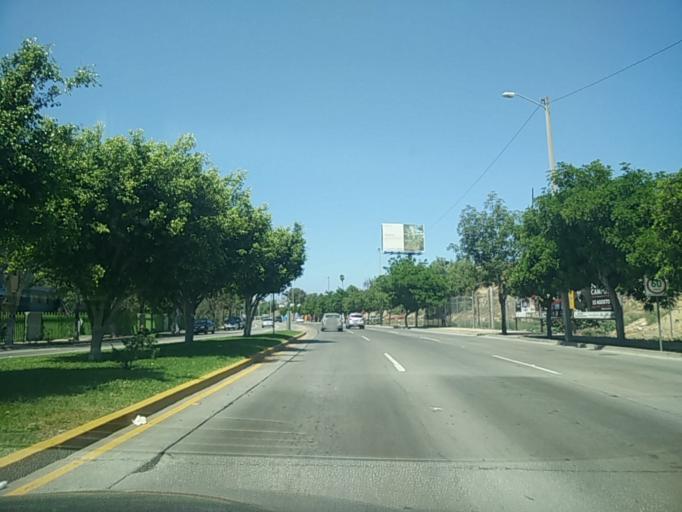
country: MX
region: Baja California
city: Tijuana
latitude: 32.5360
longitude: -117.0176
